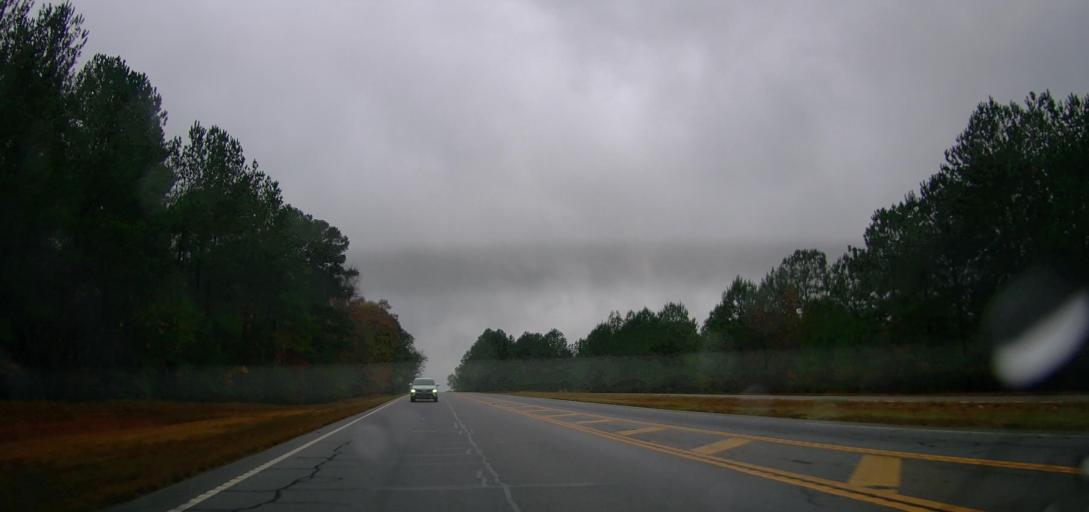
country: US
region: Georgia
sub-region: Oconee County
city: Watkinsville
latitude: 33.8423
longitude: -83.4252
